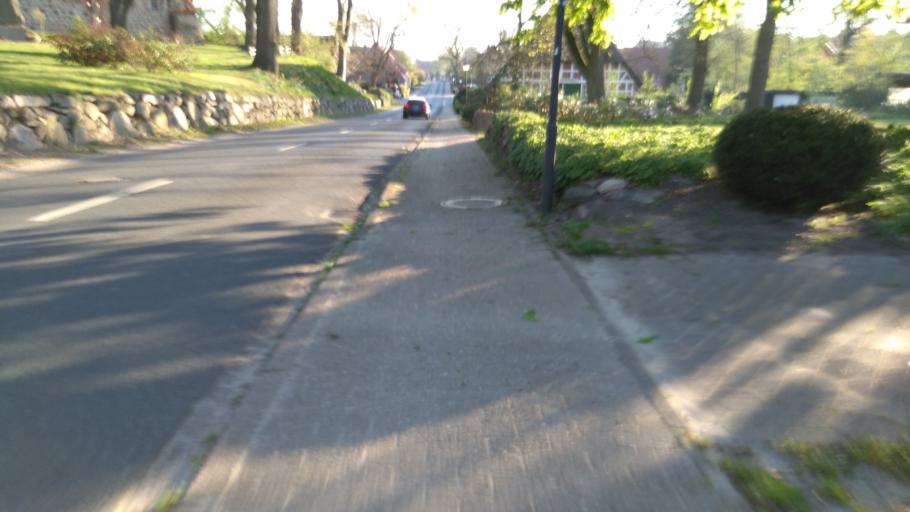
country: DE
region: Lower Saxony
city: Bliedersdorf
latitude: 53.4805
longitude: 9.5683
